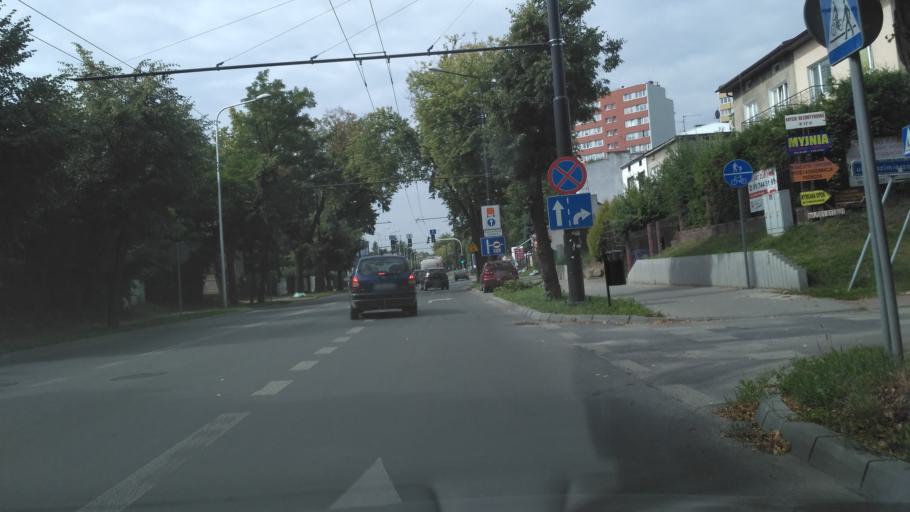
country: PL
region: Lublin Voivodeship
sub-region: Powiat lubelski
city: Lublin
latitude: 51.2129
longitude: 22.5766
